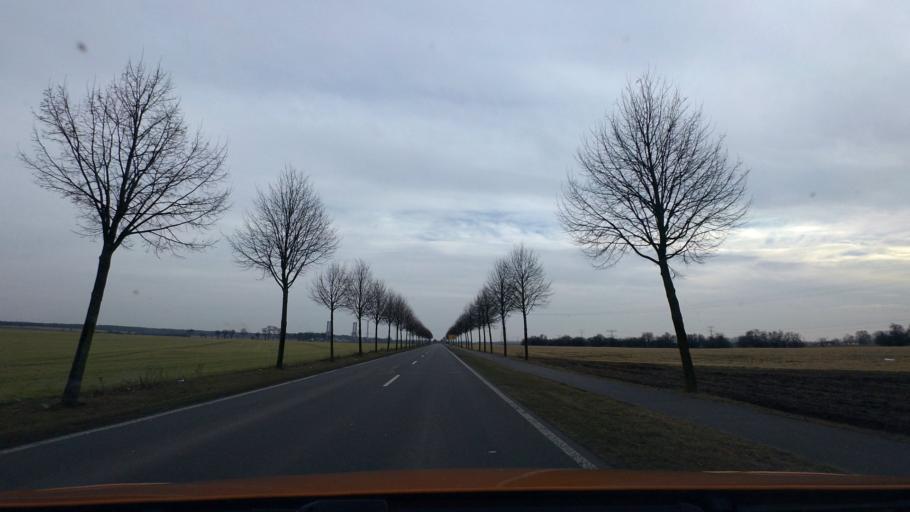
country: DE
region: Berlin
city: Falkenberg
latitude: 52.5953
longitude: 13.5430
